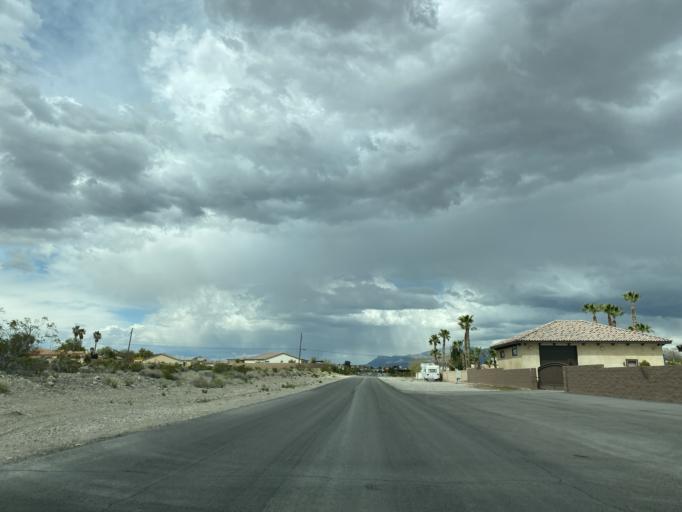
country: US
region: Nevada
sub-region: Clark County
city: Summerlin South
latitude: 36.2684
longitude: -115.3150
